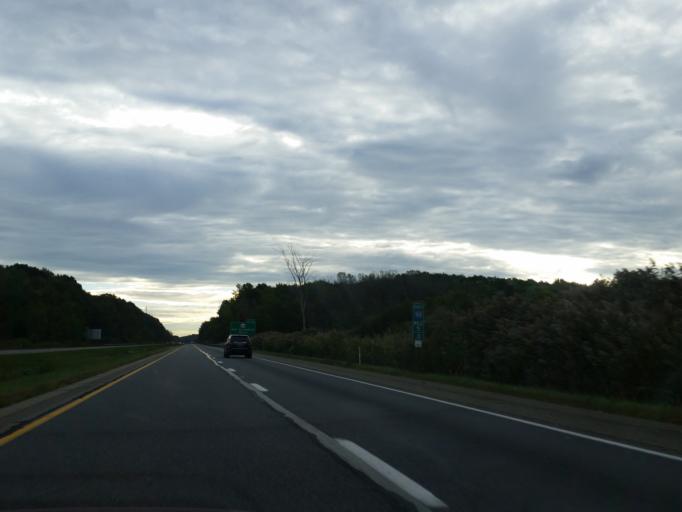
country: US
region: Pennsylvania
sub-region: Erie County
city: Albion
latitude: 41.9434
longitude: -80.4251
